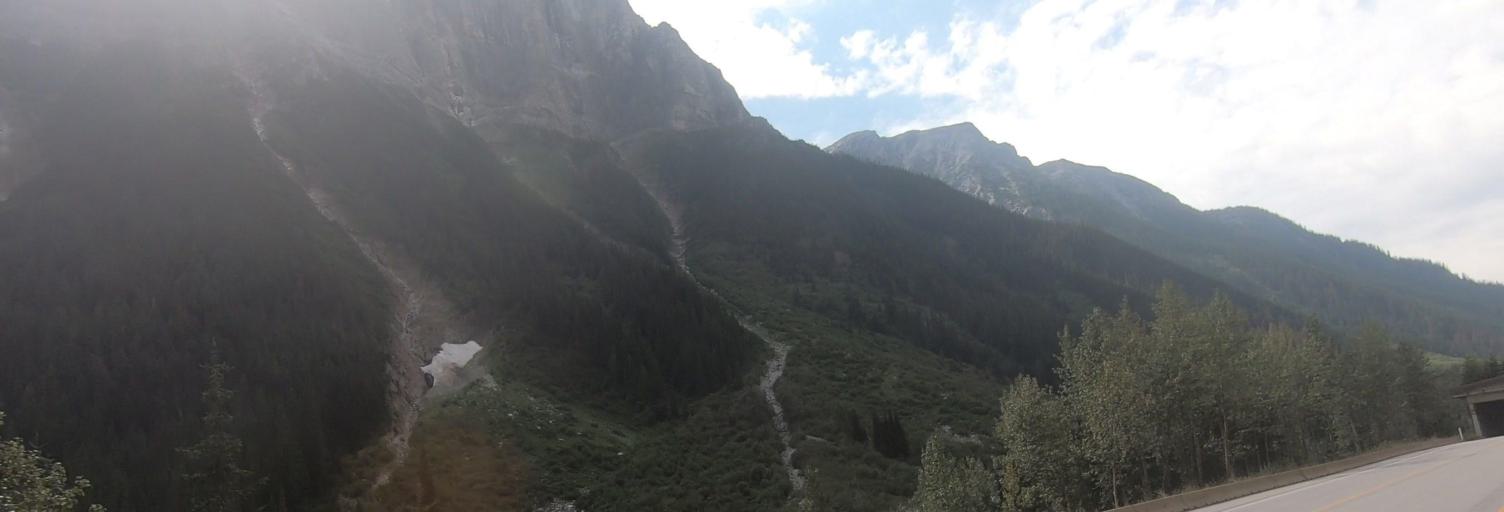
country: CA
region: British Columbia
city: Golden
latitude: 51.3254
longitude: -117.4765
